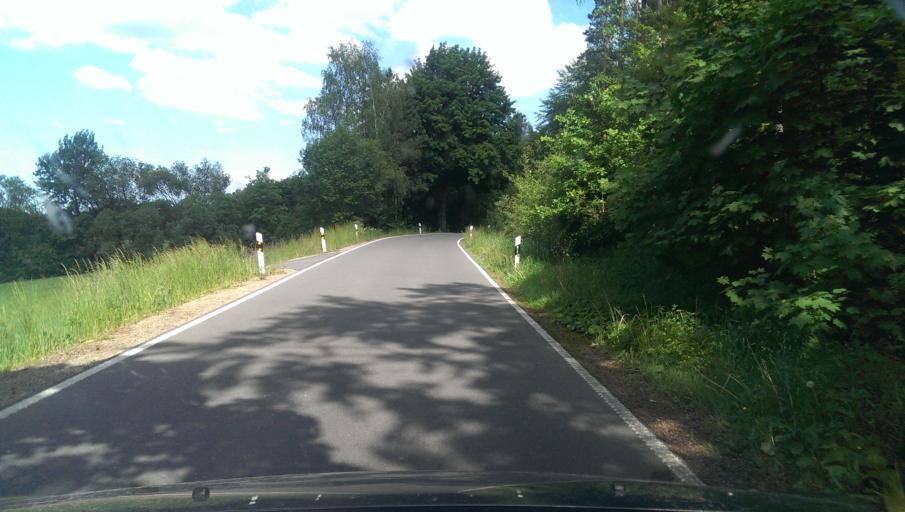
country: DE
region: Thuringia
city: Martinroda
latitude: 50.7211
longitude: 10.8987
